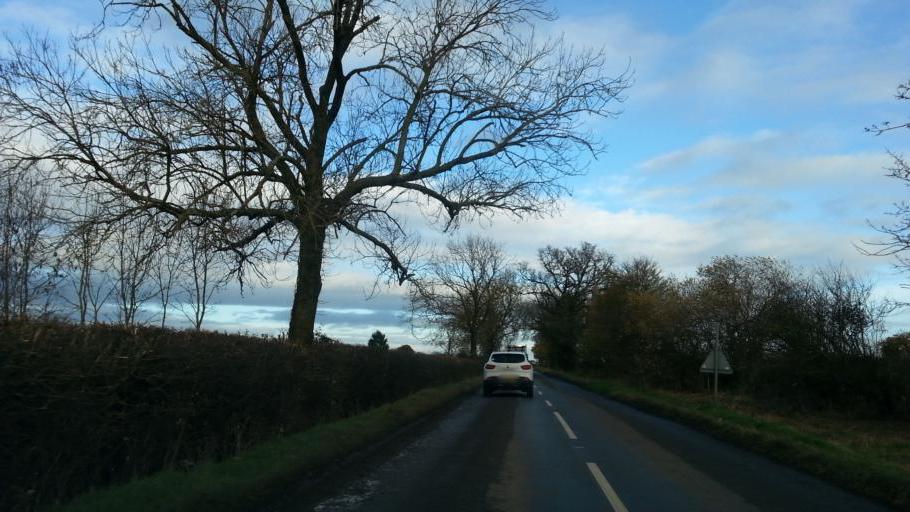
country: GB
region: England
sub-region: Oxfordshire
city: Faringdon
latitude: 51.6313
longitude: -1.5625
